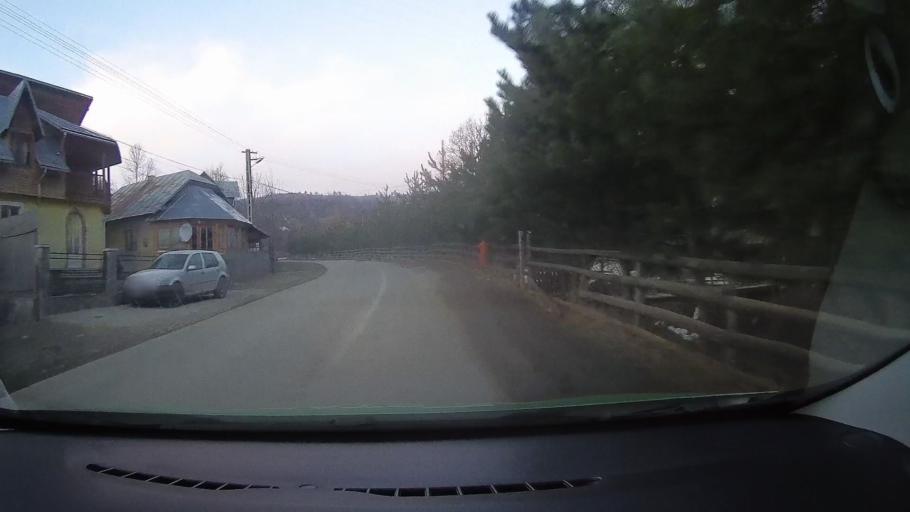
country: RO
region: Prahova
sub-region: Comuna Secaria
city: Secaria
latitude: 45.2753
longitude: 25.6870
